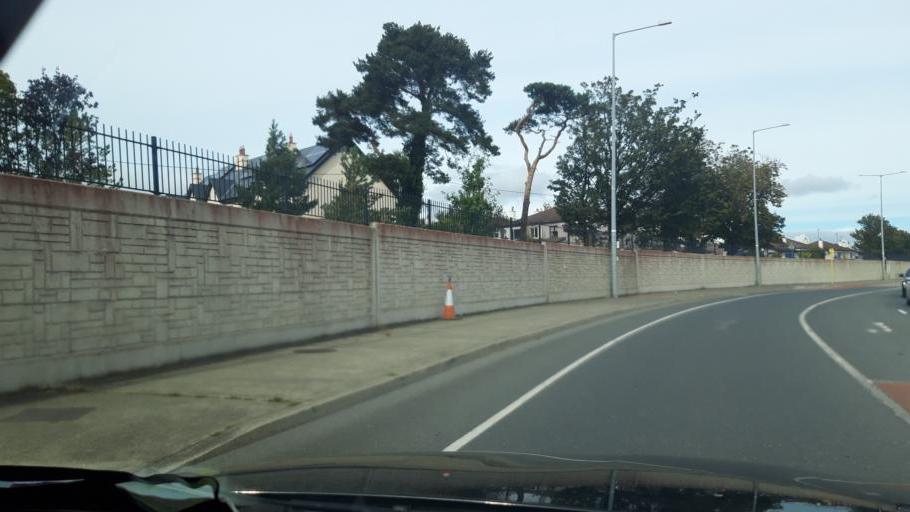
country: IE
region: Leinster
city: Sandyford
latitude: 53.2650
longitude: -6.2110
